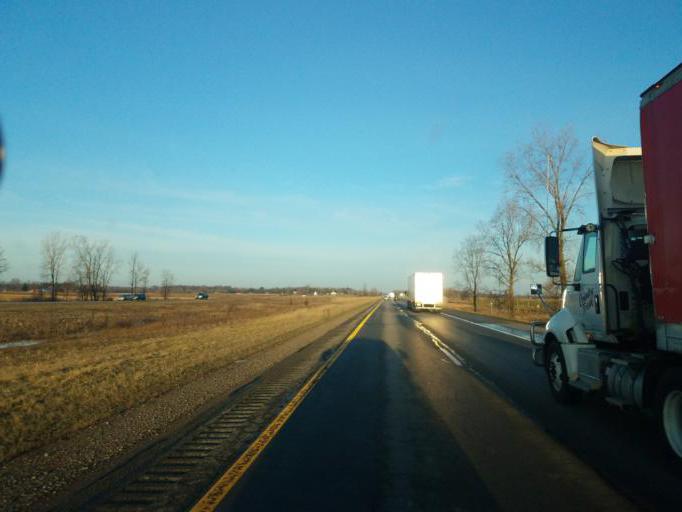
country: US
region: Michigan
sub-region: Livingston County
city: Fowlerville
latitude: 42.6510
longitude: -84.1170
